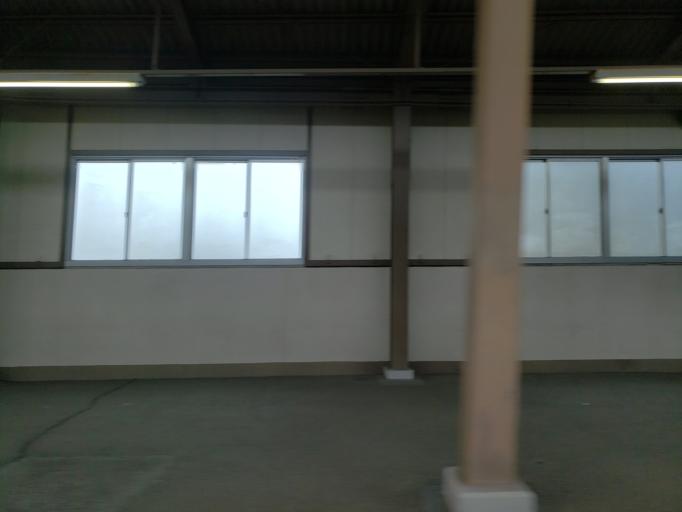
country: JP
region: Hyogo
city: Amagasaki
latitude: 34.7187
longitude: 135.4384
